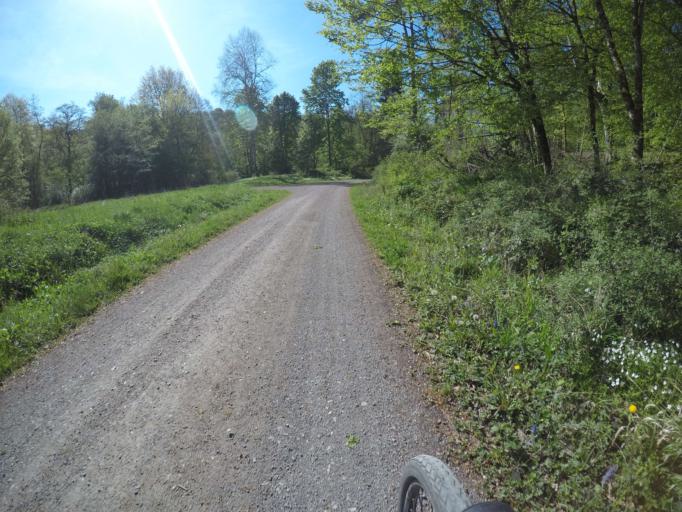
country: DE
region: Baden-Wuerttemberg
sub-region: Tuebingen Region
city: Dettenhausen
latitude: 48.5695
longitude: 9.0955
